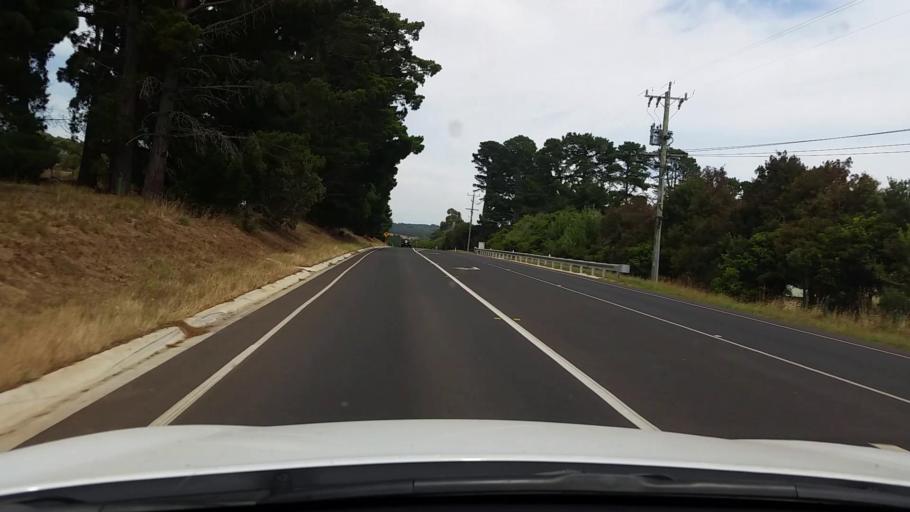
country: AU
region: Victoria
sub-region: Mornington Peninsula
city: Merricks
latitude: -38.4028
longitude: 145.0735
